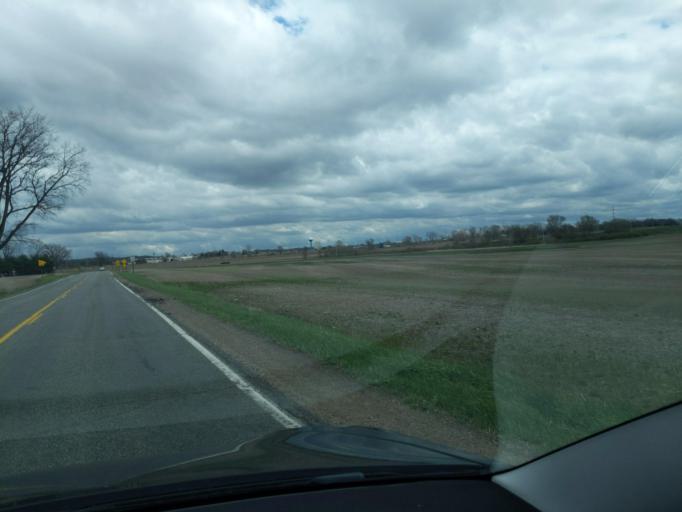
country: US
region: Michigan
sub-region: Ingham County
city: Mason
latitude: 42.5628
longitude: -84.4662
